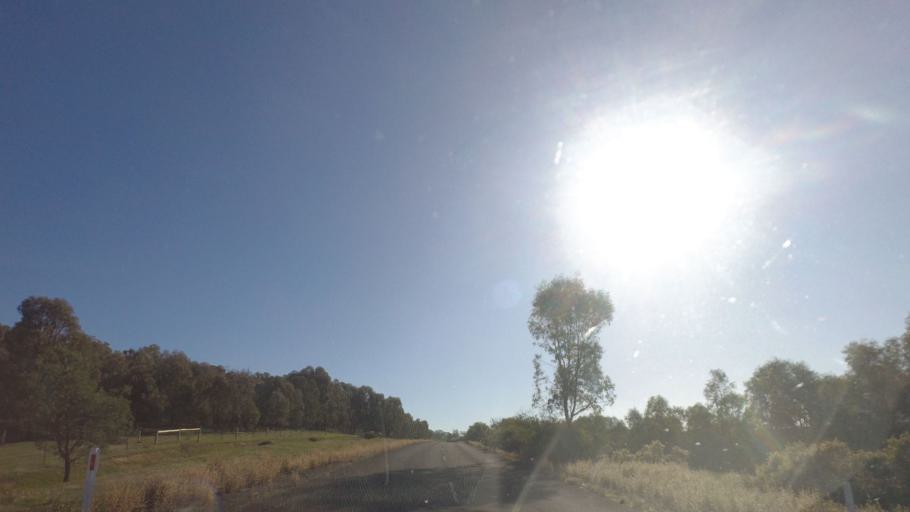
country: AU
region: Victoria
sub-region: Mount Alexander
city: Castlemaine
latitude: -37.0412
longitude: 144.2796
